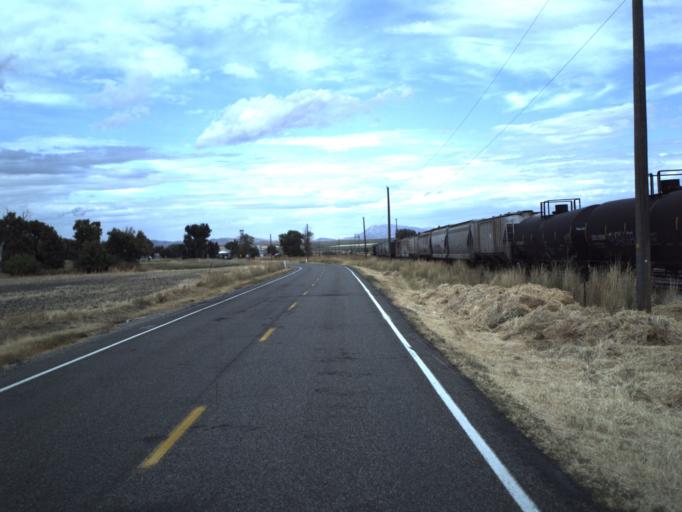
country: US
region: Utah
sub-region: Cache County
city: Benson
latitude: 41.8281
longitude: -112.0007
